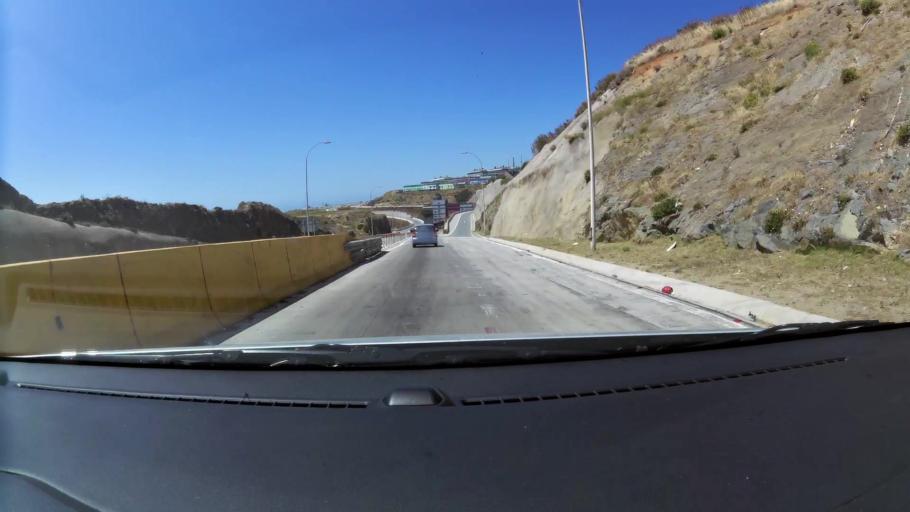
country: CL
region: Valparaiso
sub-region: Provincia de Valparaiso
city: Valparaiso
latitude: -33.0318
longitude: -71.6553
